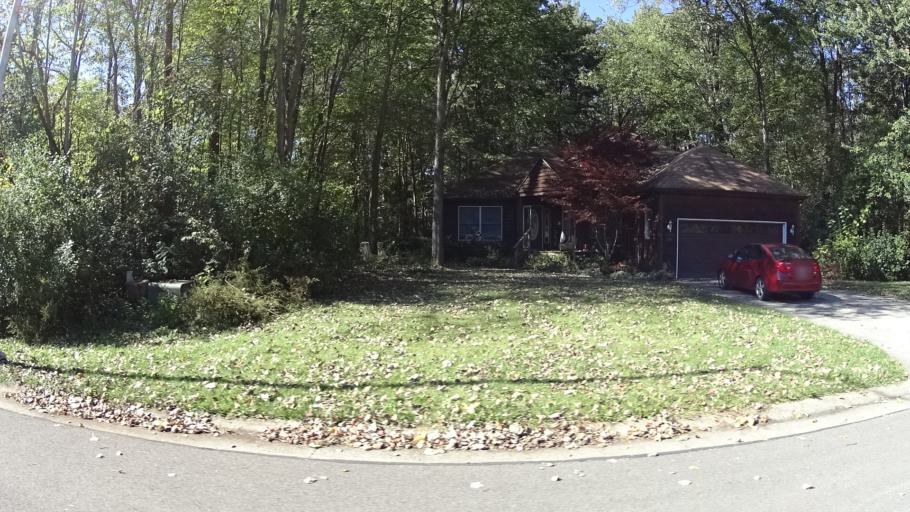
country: US
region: Ohio
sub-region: Lorain County
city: Oberlin
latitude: 41.3008
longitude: -82.2279
